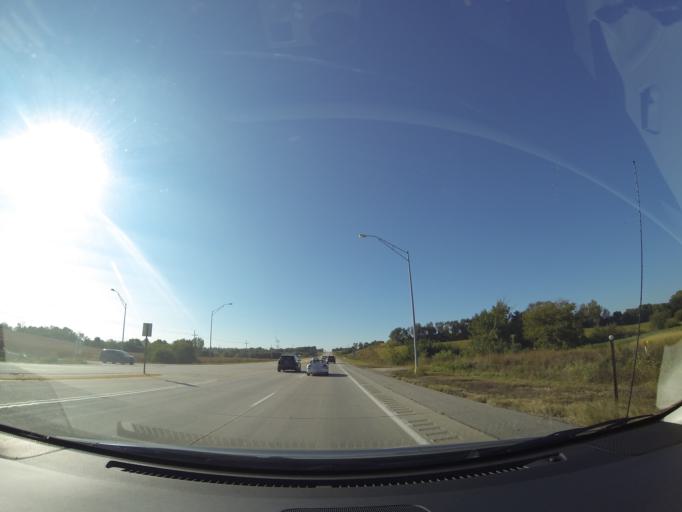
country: US
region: Nebraska
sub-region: Sarpy County
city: Gretna
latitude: 41.1763
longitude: -96.2343
